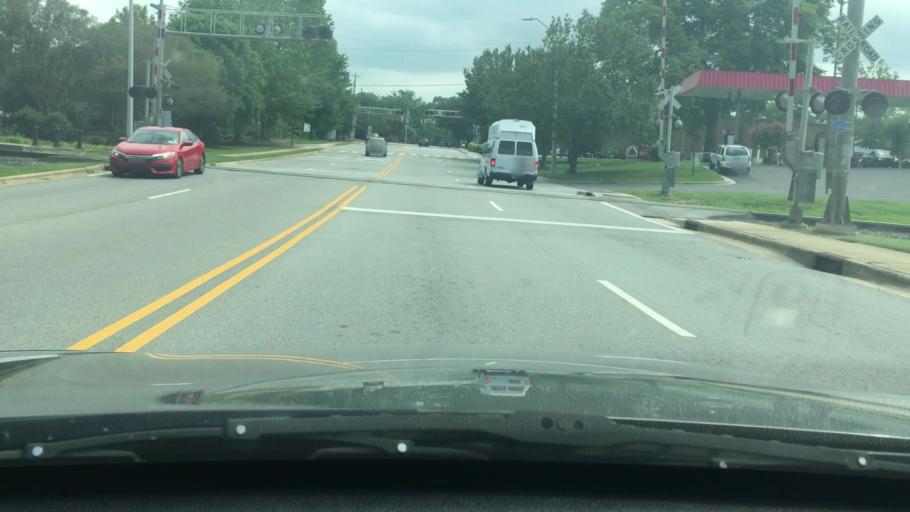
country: US
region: North Carolina
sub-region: Wake County
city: Cary
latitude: 35.7893
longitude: -78.7833
